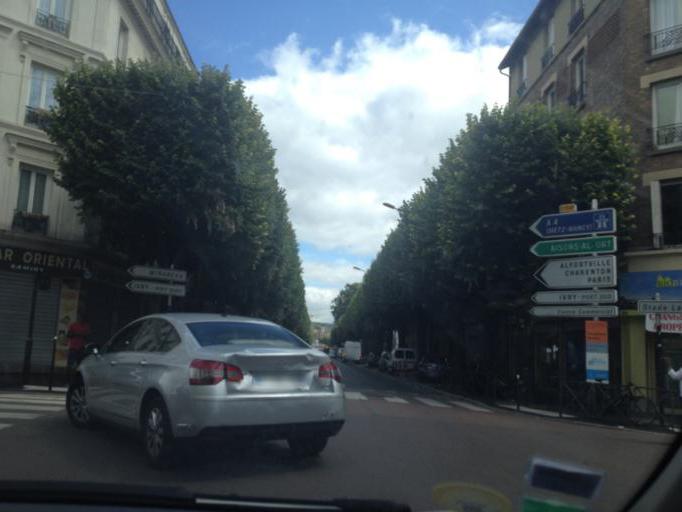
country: FR
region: Ile-de-France
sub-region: Departement du Val-de-Marne
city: Ivry-sur-Seine
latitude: 48.8166
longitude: 2.3953
